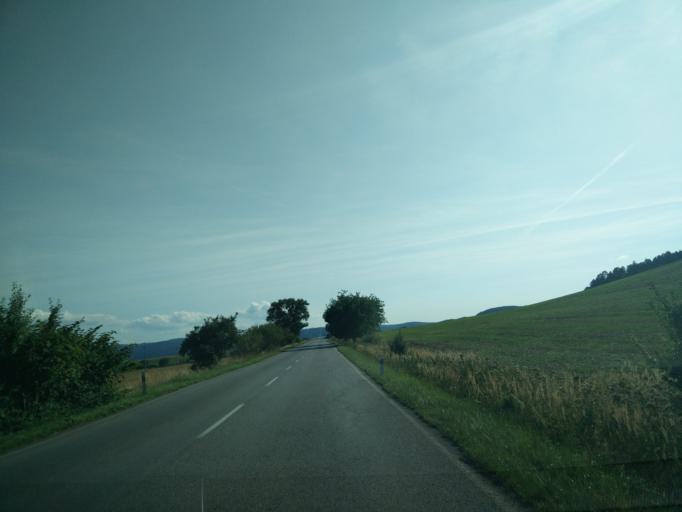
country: SK
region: Nitriansky
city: Handlova
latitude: 48.9247
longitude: 18.7788
